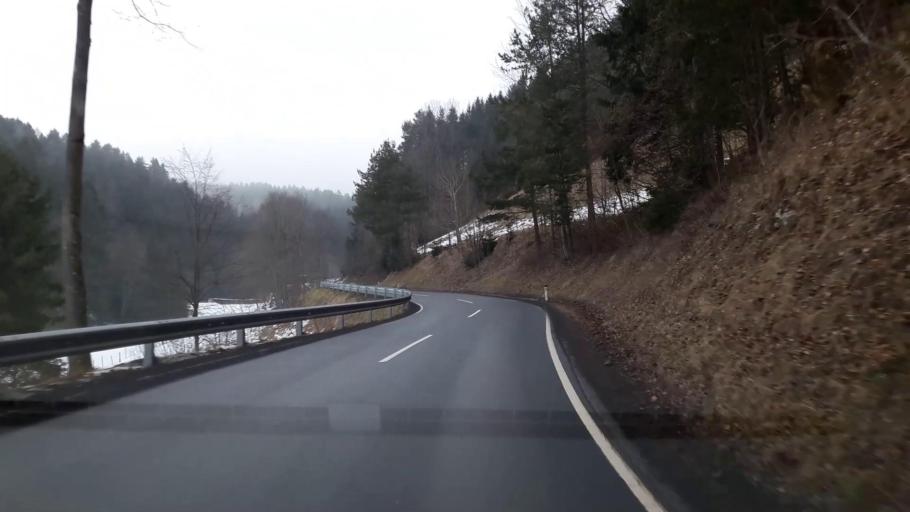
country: AT
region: Lower Austria
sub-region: Politischer Bezirk Neunkirchen
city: Feistritz am Wechsel
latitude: 47.5614
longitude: 16.0538
